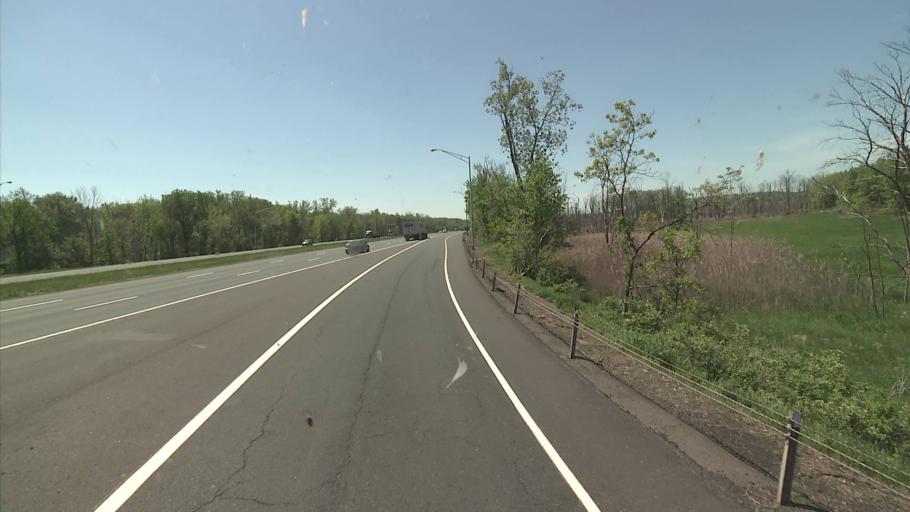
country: US
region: Connecticut
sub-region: Hartford County
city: Farmington
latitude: 41.7033
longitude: -72.8046
